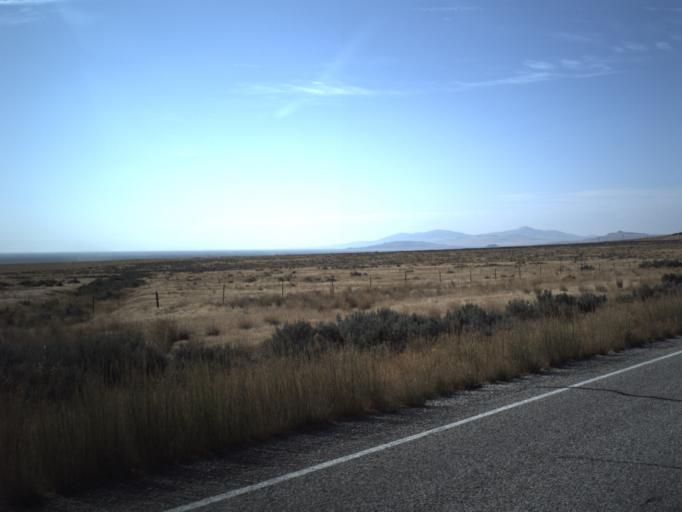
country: US
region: Idaho
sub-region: Minidoka County
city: Rupert
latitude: 41.8441
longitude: -113.1390
